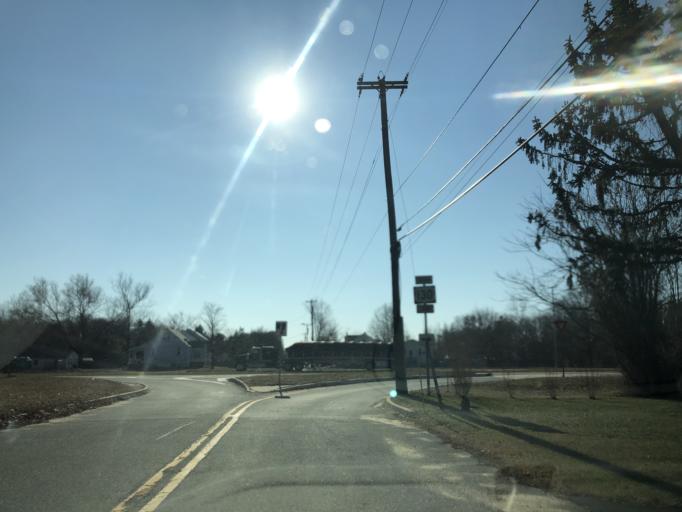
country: US
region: Pennsylvania
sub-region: Delaware County
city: Chester
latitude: 39.8036
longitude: -75.3402
